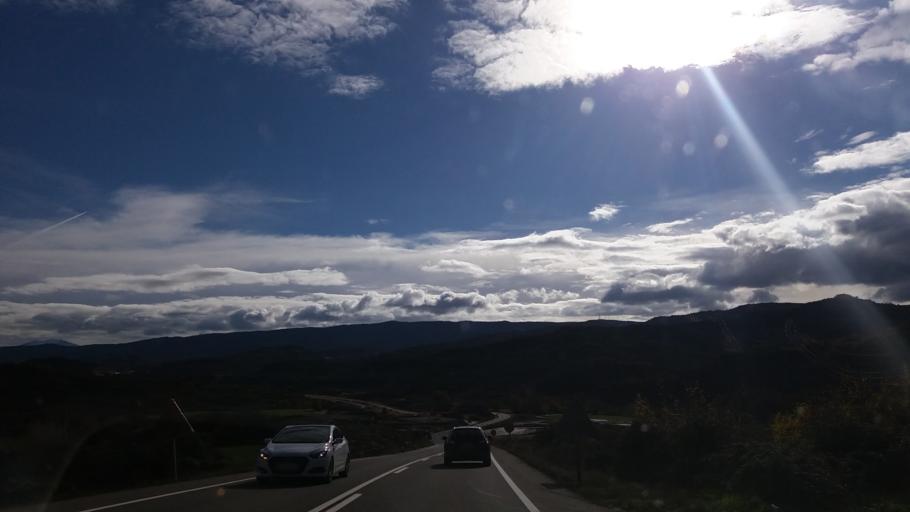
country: ES
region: Aragon
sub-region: Provincia de Huesca
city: Sabinanigo
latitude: 42.4177
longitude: -0.3945
